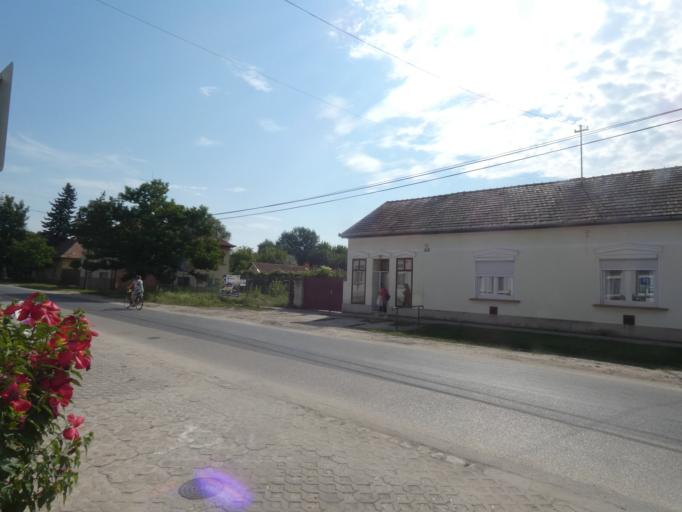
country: HU
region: Bacs-Kiskun
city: Lajosmizse
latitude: 47.0249
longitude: 19.5545
